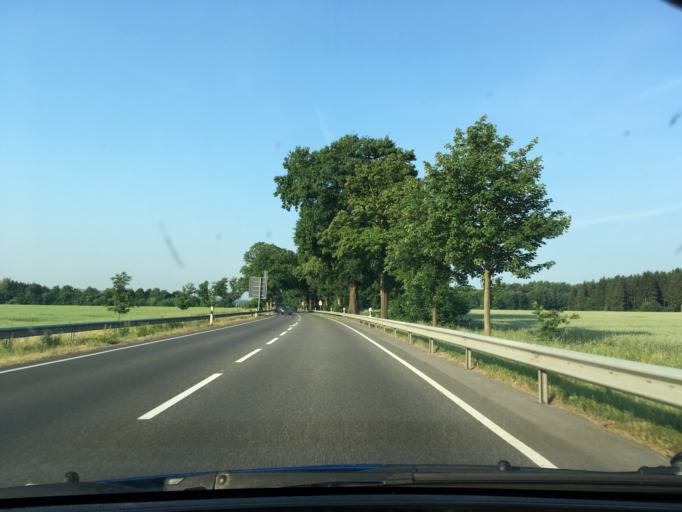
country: DE
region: Lower Saxony
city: Buchholz in der Nordheide
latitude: 53.3588
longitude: 9.8669
